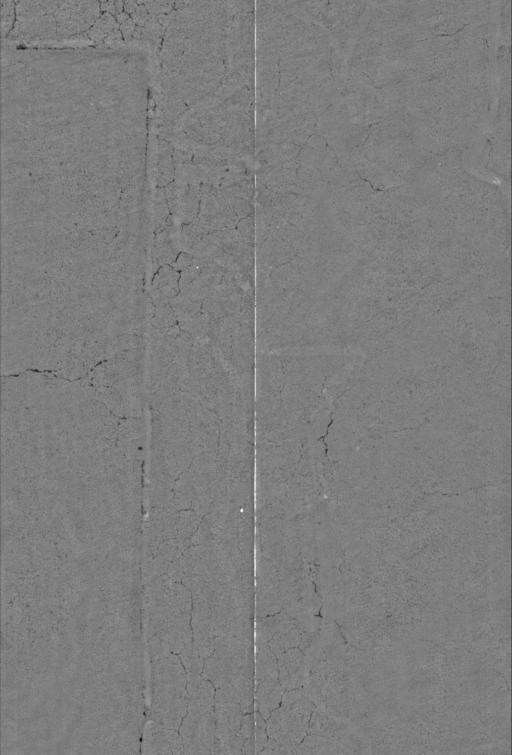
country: US
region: Maryland
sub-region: Prince George's County
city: Hillcrest Heights
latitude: 38.8619
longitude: -76.9732
